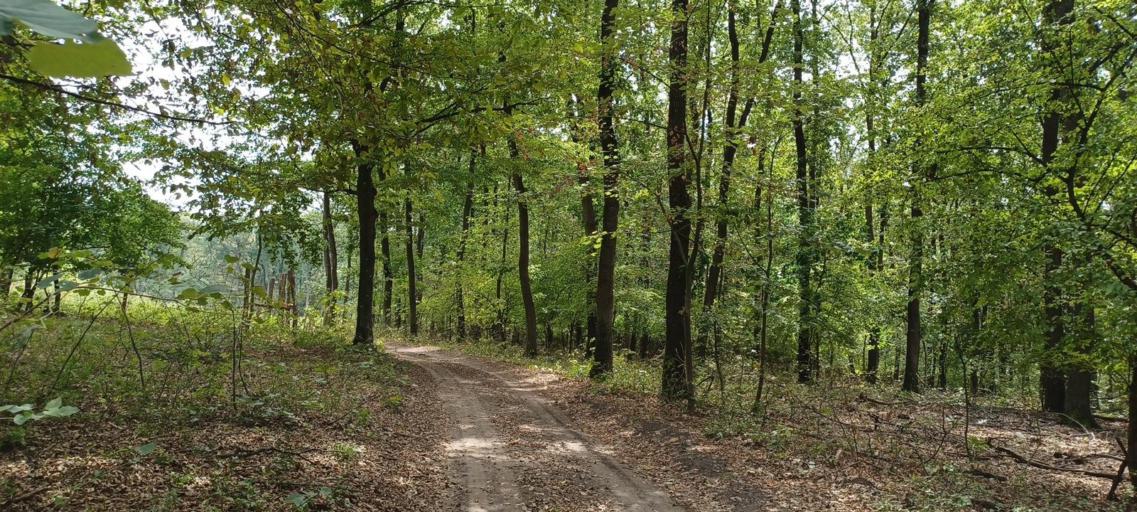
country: HU
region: Tolna
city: Szentgalpuszta
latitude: 46.3325
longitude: 18.6268
